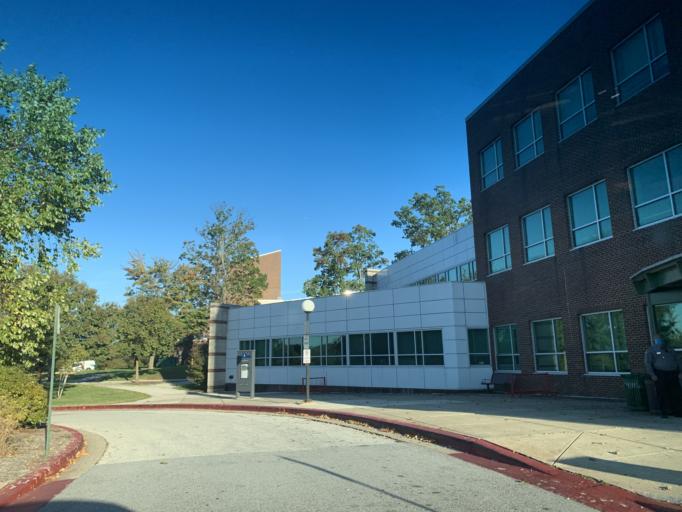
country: US
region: Maryland
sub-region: Baltimore County
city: Rossville
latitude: 39.3543
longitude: -76.4818
